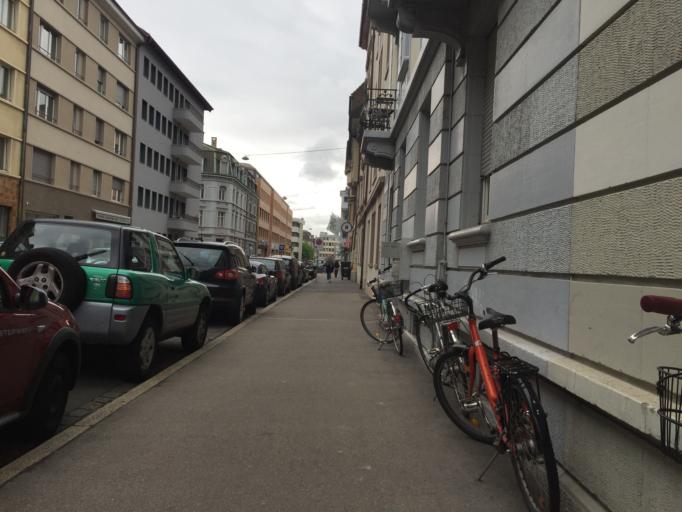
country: CH
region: Basel-City
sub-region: Basel-Stadt
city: Basel
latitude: 47.5443
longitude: 7.5960
